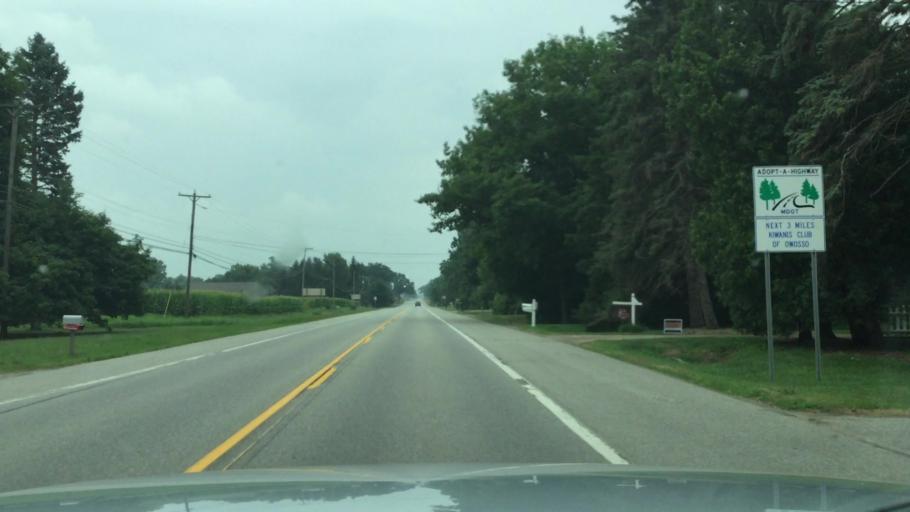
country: US
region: Michigan
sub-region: Shiawassee County
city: New Haven
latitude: 43.0552
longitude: -84.1773
